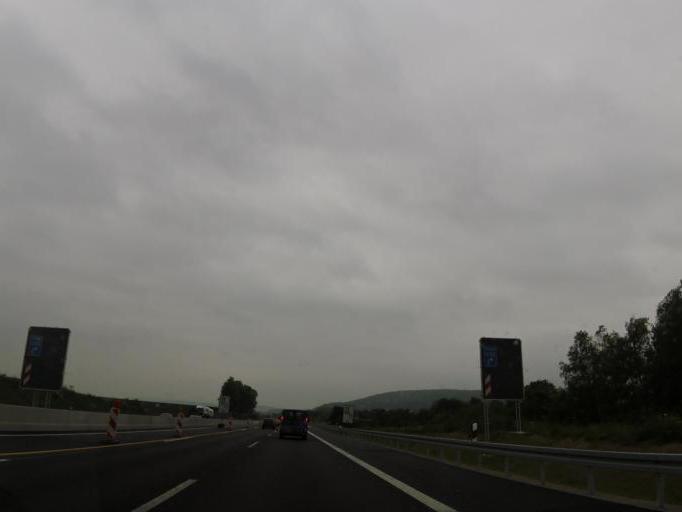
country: DE
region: Lower Saxony
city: Seesen
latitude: 51.8963
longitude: 10.1322
